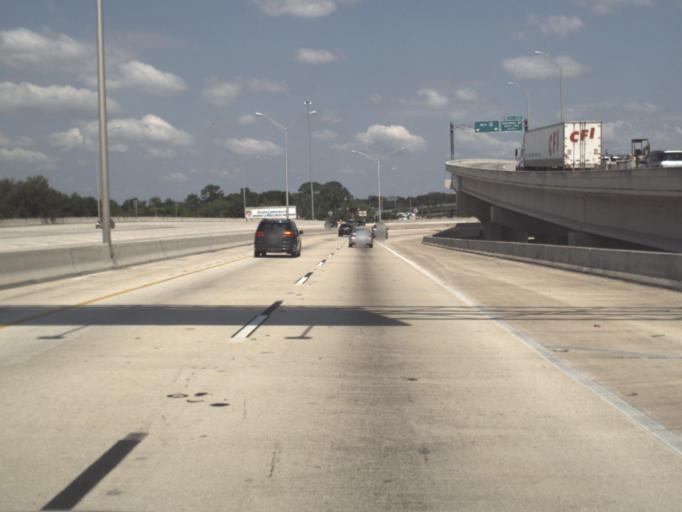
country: US
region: Florida
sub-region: Duval County
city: Jacksonville
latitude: 30.3179
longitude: -81.6789
